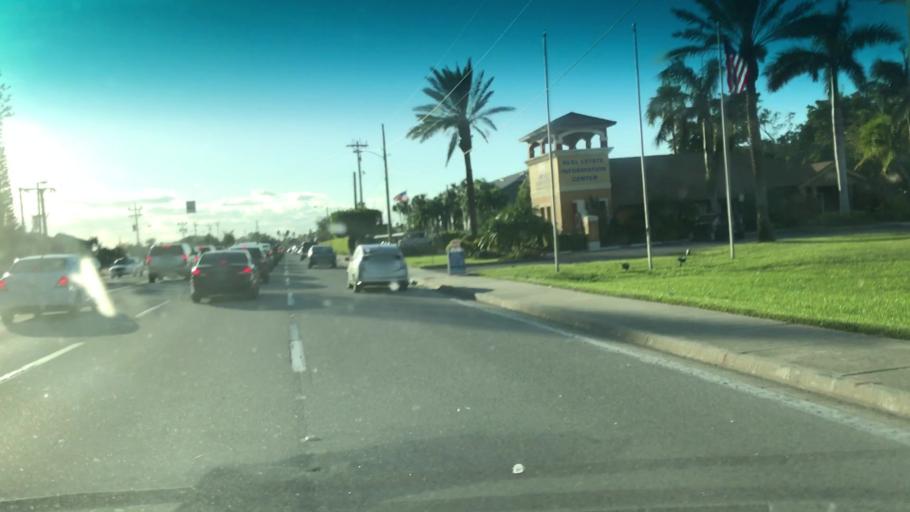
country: US
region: Florida
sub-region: Lee County
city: Cape Coral
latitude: 26.5627
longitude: -81.9376
